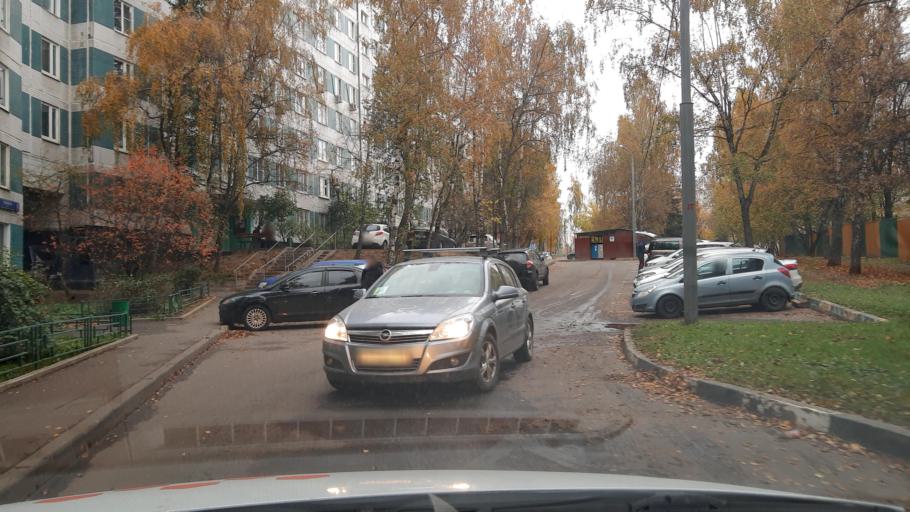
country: RU
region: Moscow
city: Orekhovo-Borisovo
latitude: 55.5985
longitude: 37.7180
